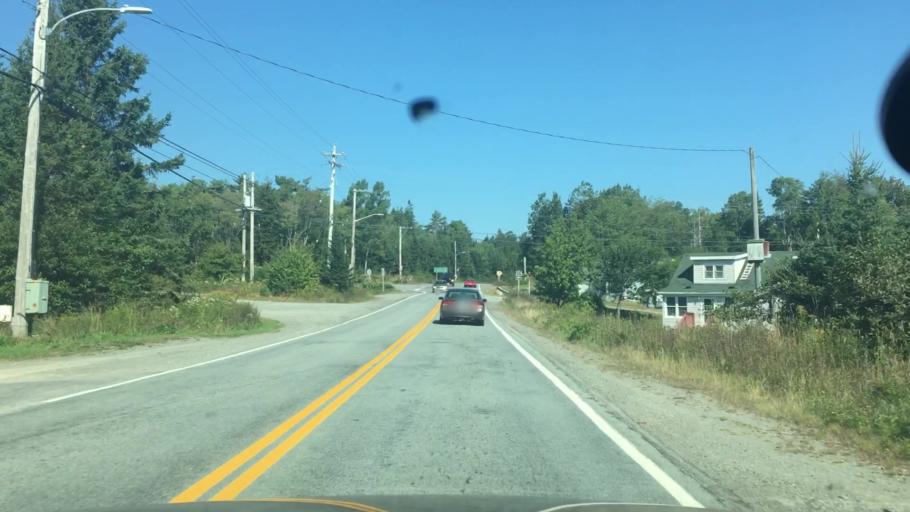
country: CA
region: Nova Scotia
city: New Glasgow
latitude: 44.9249
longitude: -62.5458
